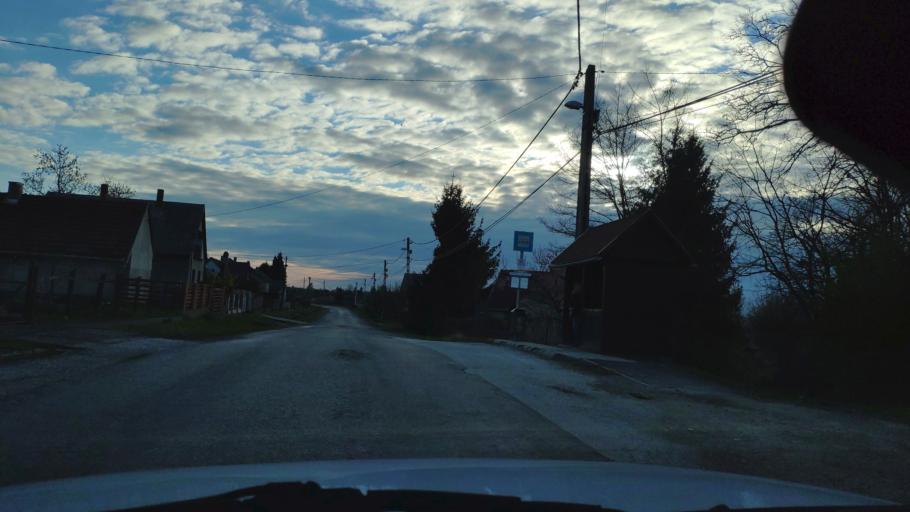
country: HU
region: Zala
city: Nagykanizsa
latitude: 46.4321
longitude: 17.0582
